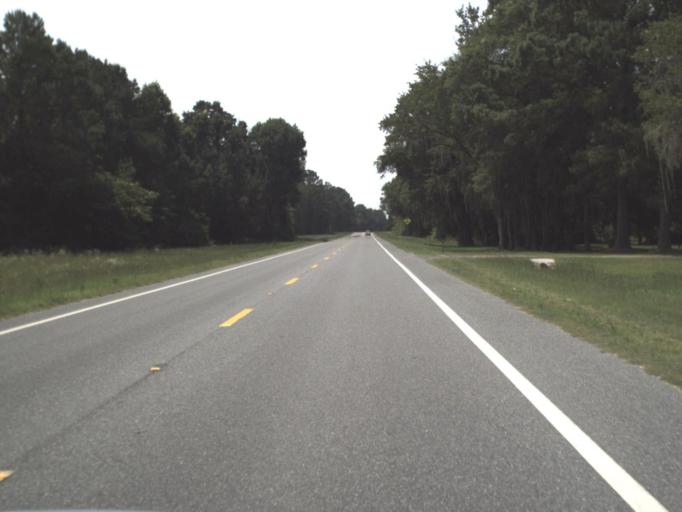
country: US
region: Florida
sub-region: Hamilton County
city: Jasper
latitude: 30.5402
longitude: -83.0509
